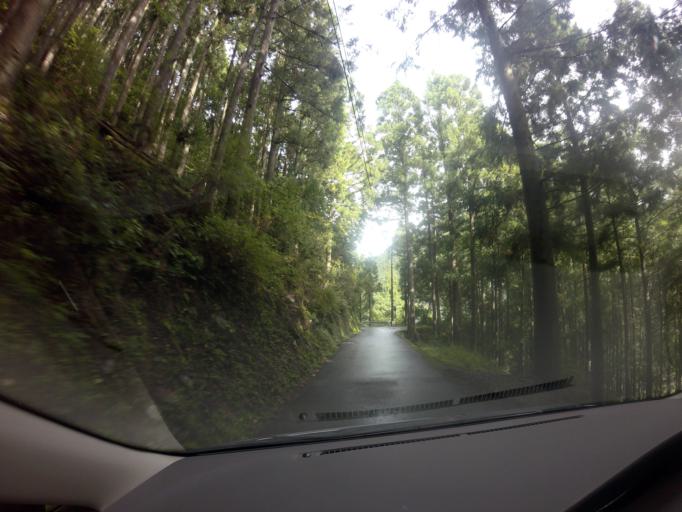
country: JP
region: Wakayama
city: Shingu
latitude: 33.9691
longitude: 135.8083
